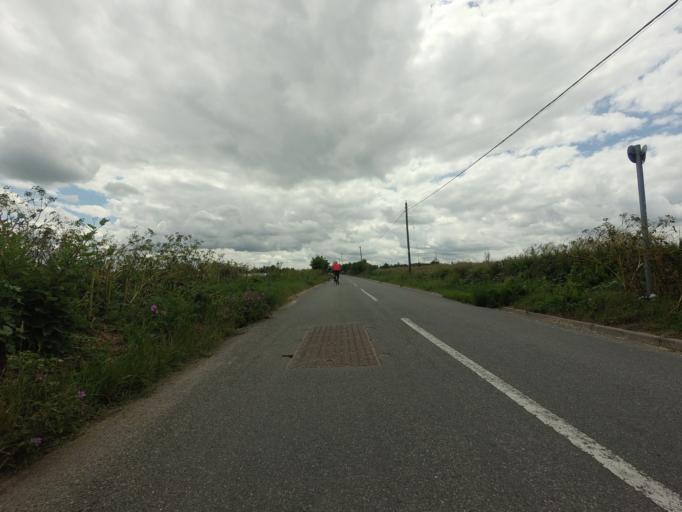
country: GB
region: England
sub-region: Medway
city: Allhallows
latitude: 51.4611
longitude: 0.6382
